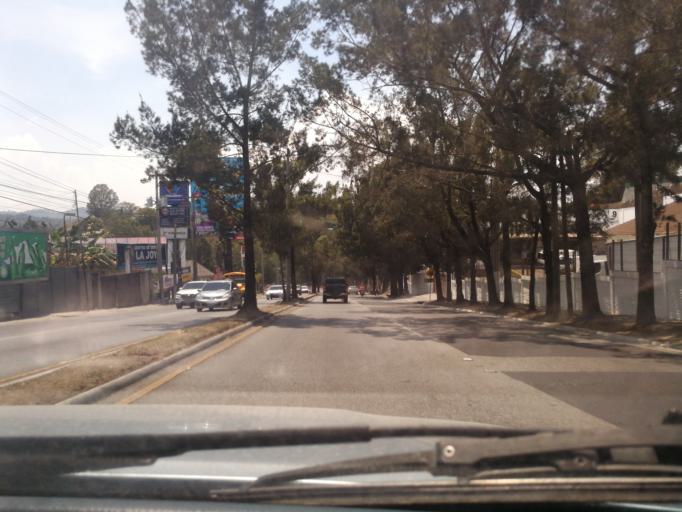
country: GT
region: Guatemala
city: Guatemala City
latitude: 14.6213
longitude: -90.4964
